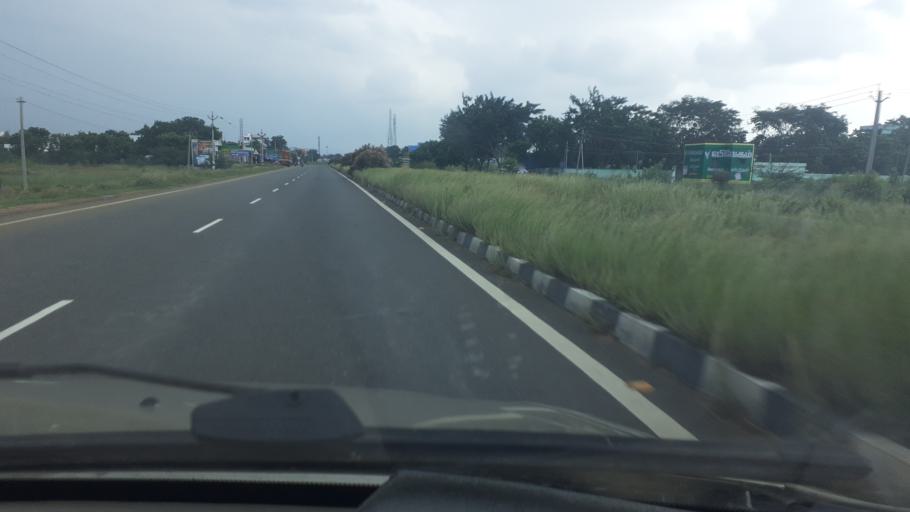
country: IN
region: Tamil Nadu
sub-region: Madurai
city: Kallupatti
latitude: 9.7039
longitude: 77.9733
